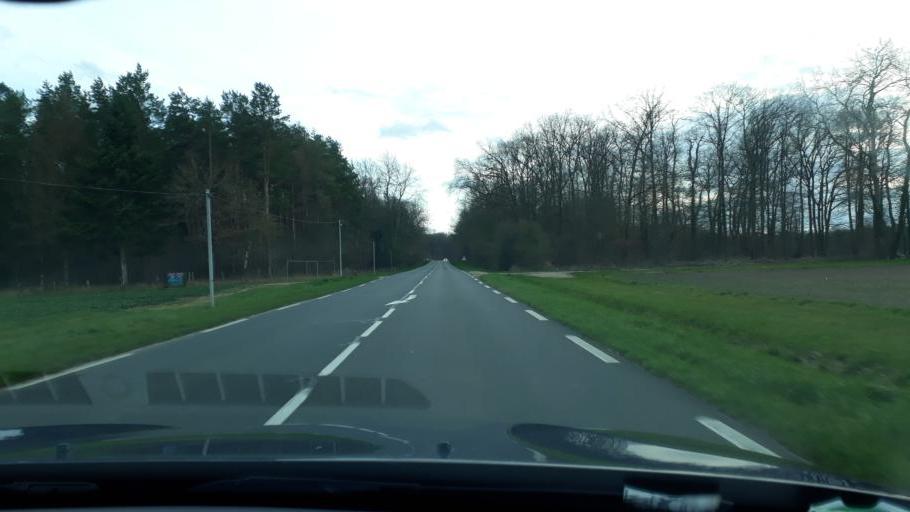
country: FR
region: Centre
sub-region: Departement du Loiret
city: Chilleurs-aux-Bois
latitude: 48.0568
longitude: 2.1290
